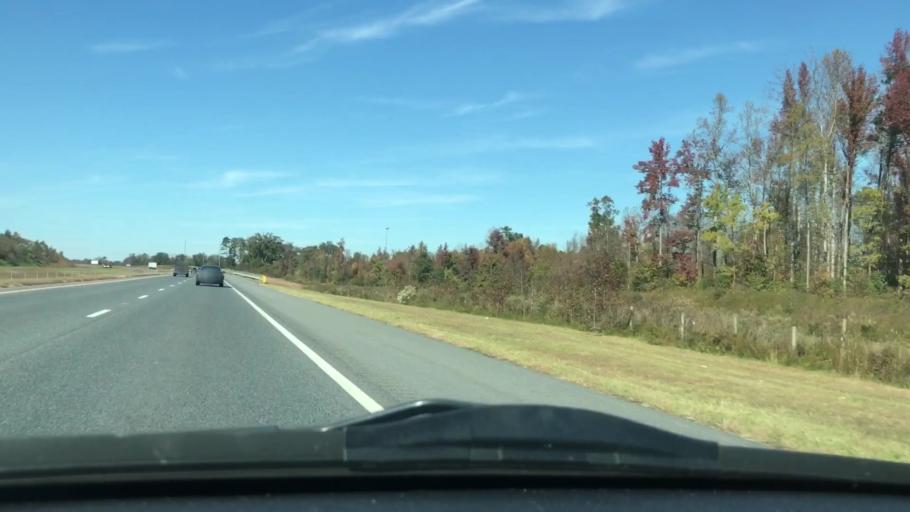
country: US
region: North Carolina
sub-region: Randolph County
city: Randleman
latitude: 35.8382
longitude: -79.8629
